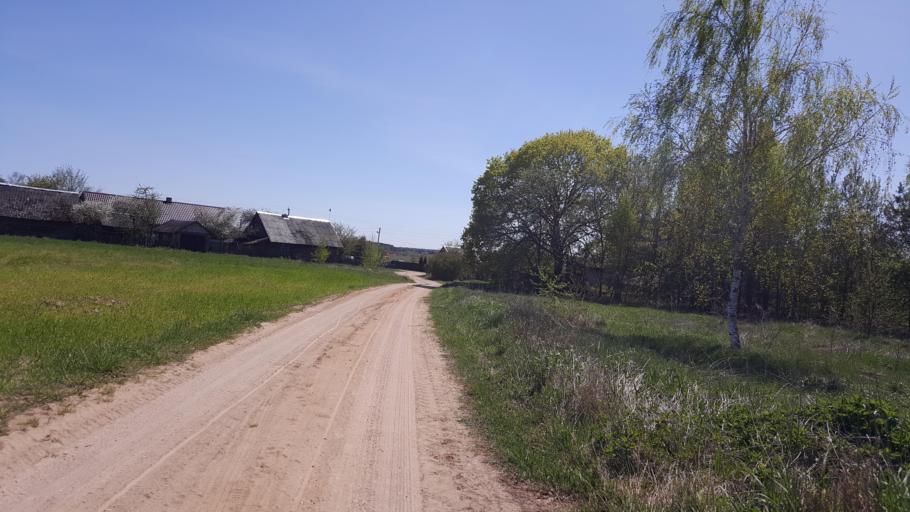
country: BY
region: Brest
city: Kamyanyets
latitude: 52.4571
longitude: 23.8783
